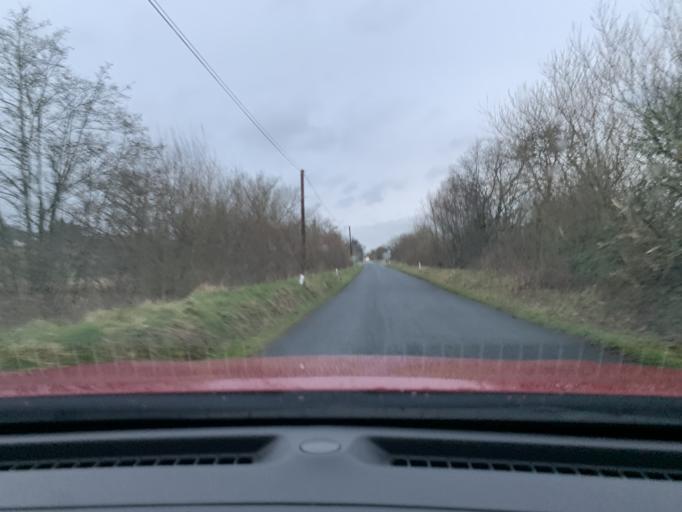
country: IE
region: Connaught
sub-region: Roscommon
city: Boyle
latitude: 54.0293
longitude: -8.3357
